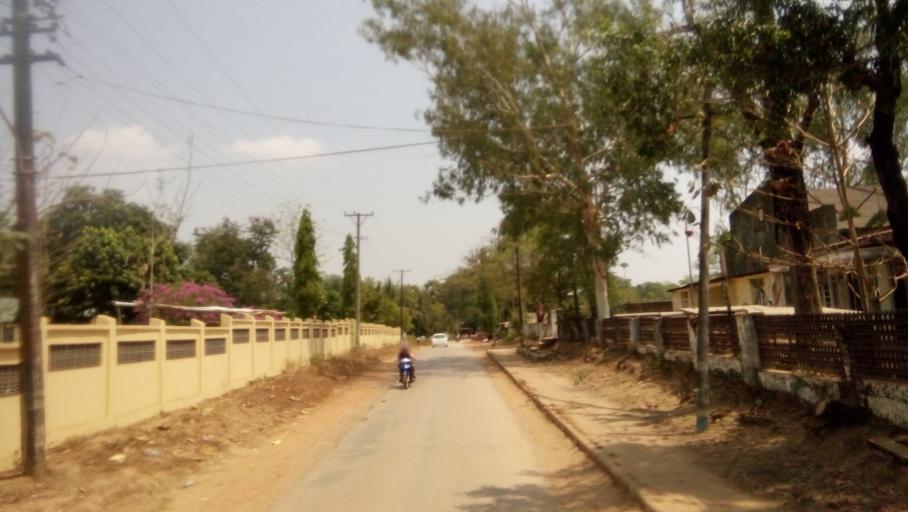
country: MM
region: Kayin
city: Hpa-an
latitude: 17.1293
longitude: 97.8185
